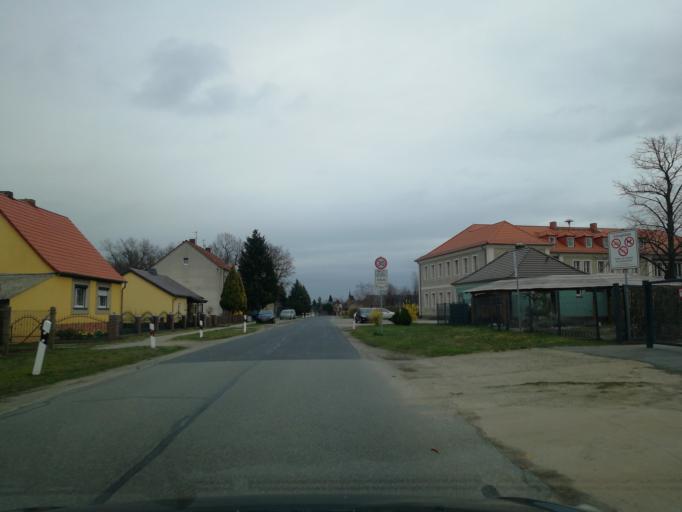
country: DE
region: Brandenburg
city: Vetschau
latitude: 51.7282
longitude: 14.0418
